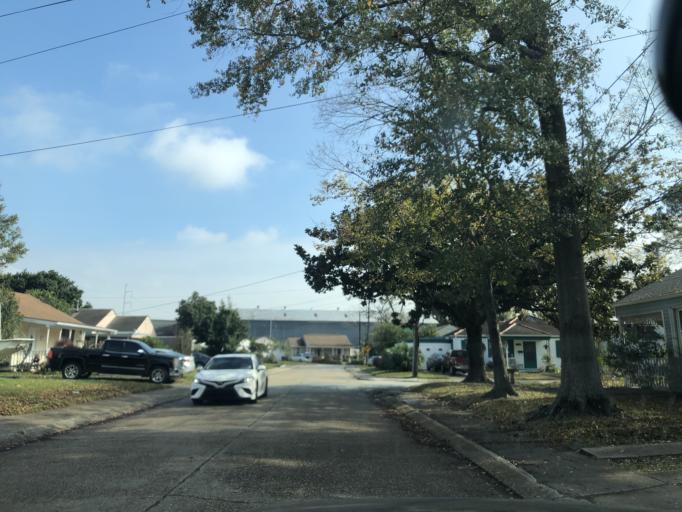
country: US
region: Louisiana
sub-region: Jefferson Parish
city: Metairie Terrace
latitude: 29.9740
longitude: -90.1668
